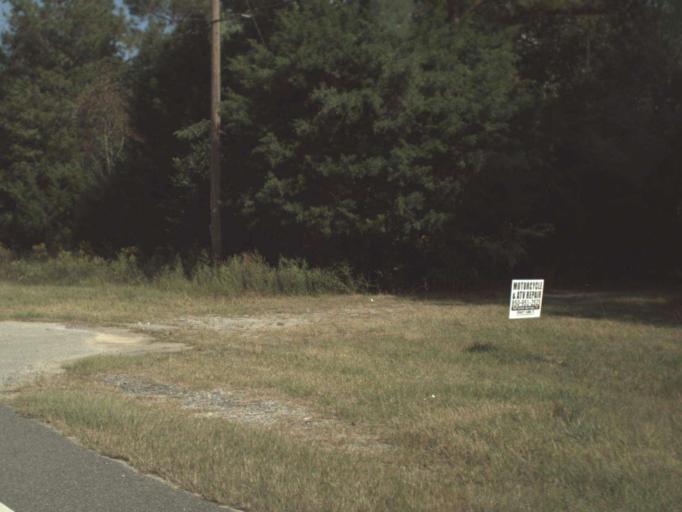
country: US
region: Florida
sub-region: Walton County
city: DeFuniak Springs
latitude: 30.7848
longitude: -86.1188
